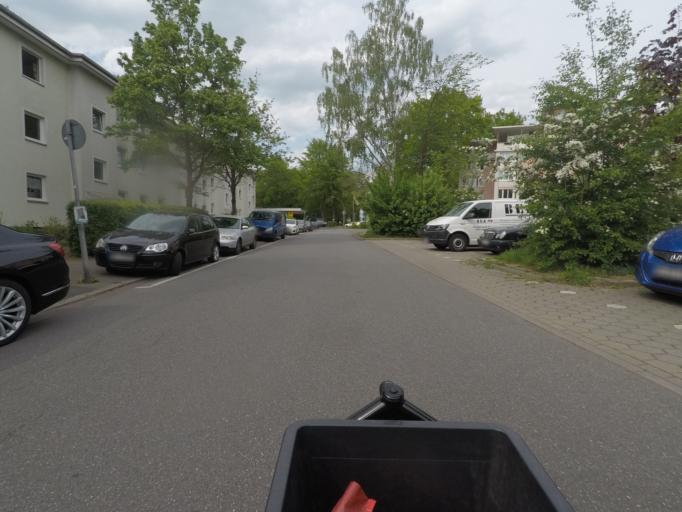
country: DE
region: Hamburg
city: Wellingsbuettel
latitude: 53.6252
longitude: 10.0920
